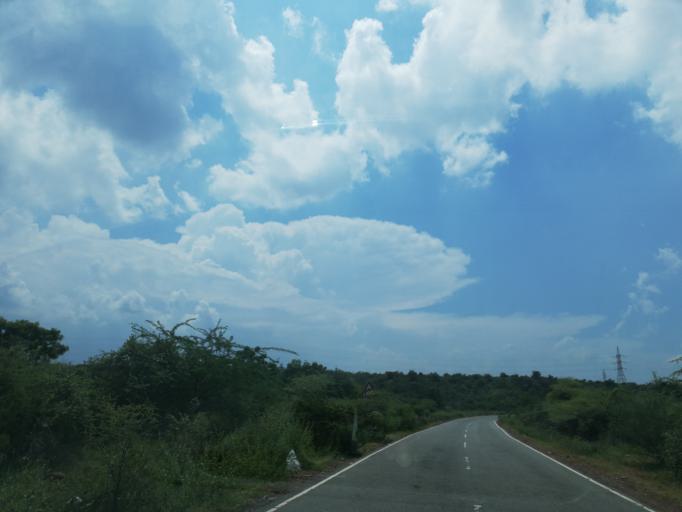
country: IN
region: Andhra Pradesh
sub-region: Guntur
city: Macherla
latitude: 16.5620
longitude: 79.3539
